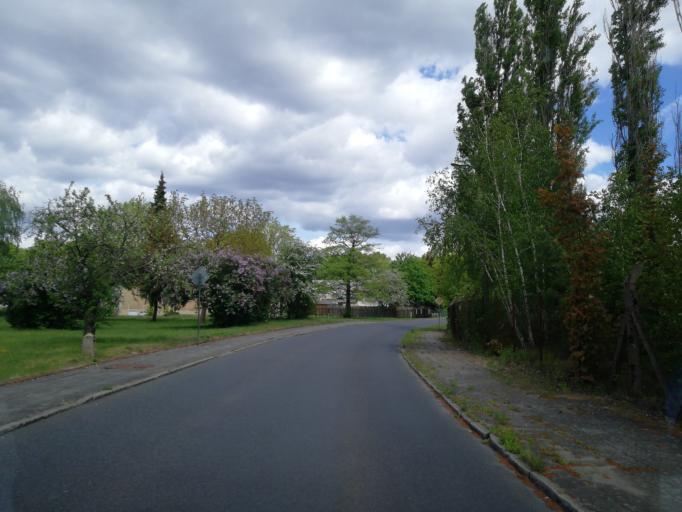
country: DE
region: Brandenburg
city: Lauchhammer
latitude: 51.5052
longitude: 13.7982
